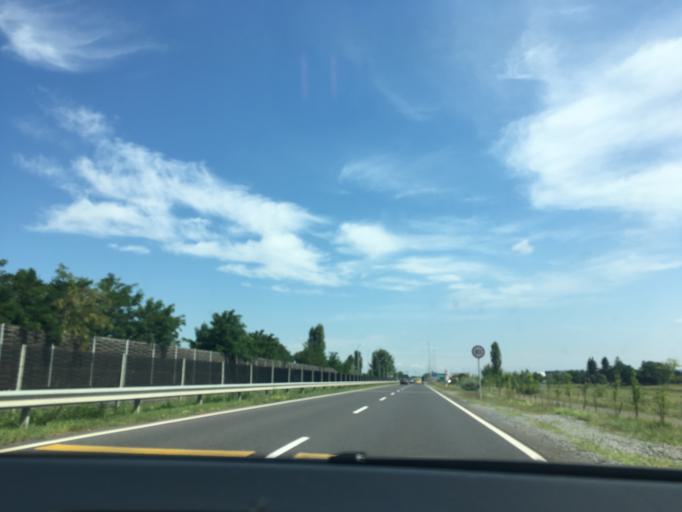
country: HU
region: Szabolcs-Szatmar-Bereg
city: Nyiregyhaza
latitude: 47.8983
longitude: 21.7110
